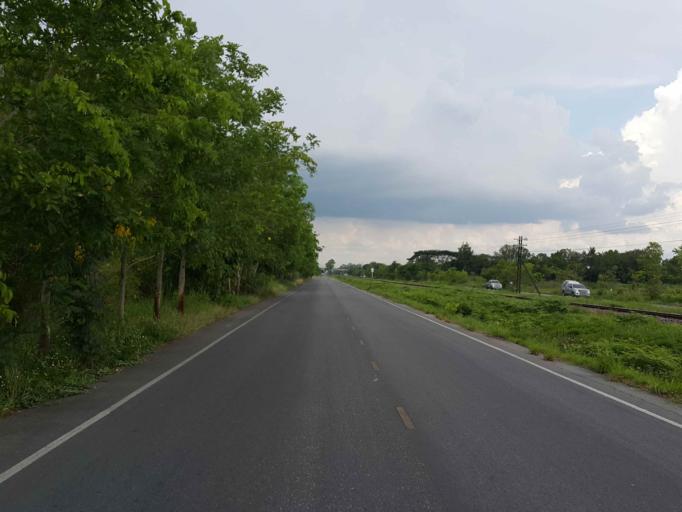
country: TH
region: Chiang Mai
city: Saraphi
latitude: 18.7419
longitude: 99.0282
